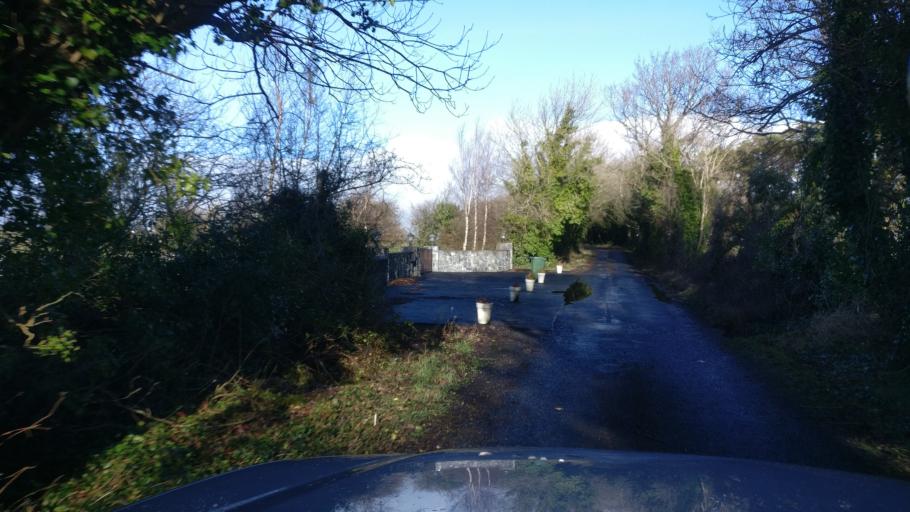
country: IE
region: Connaught
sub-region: County Galway
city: Loughrea
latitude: 53.2217
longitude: -8.6690
